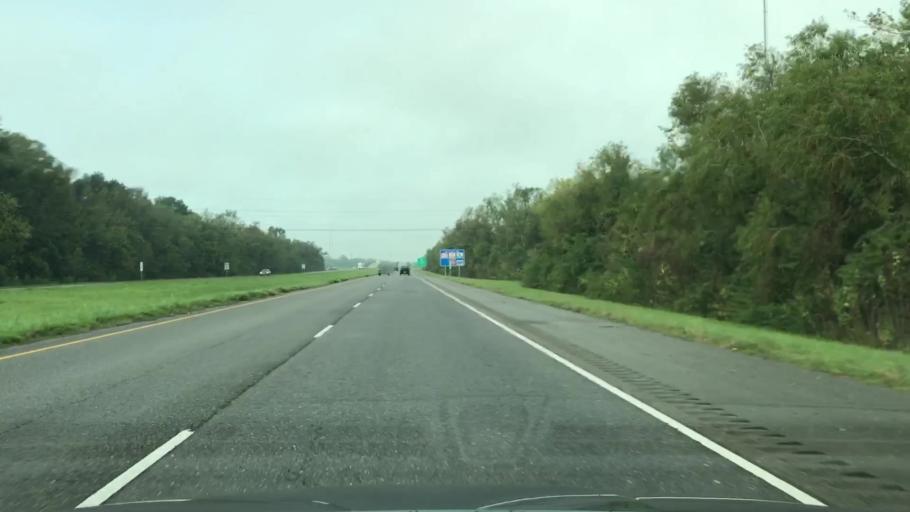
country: US
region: Louisiana
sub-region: Terrebonne Parish
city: Gray
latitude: 29.6809
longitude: -90.7721
